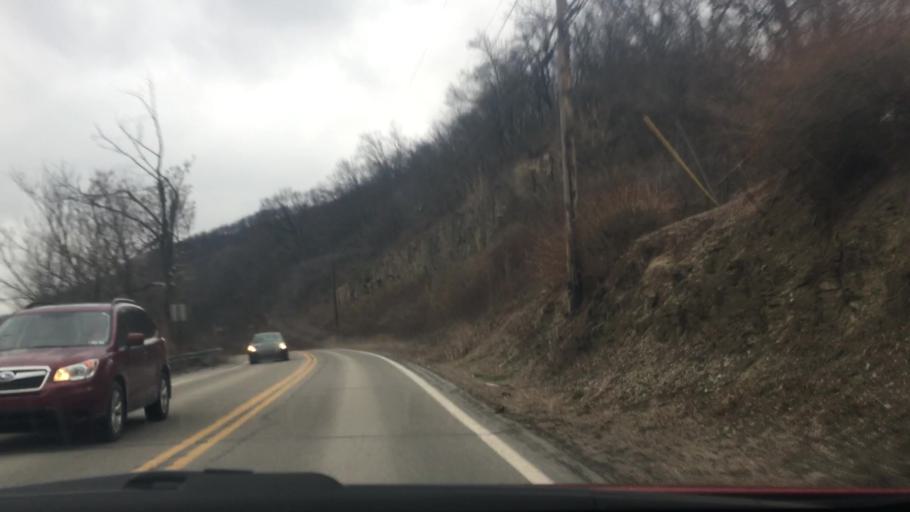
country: US
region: Pennsylvania
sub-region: Allegheny County
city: Clairton
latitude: 40.3017
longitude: -79.8662
